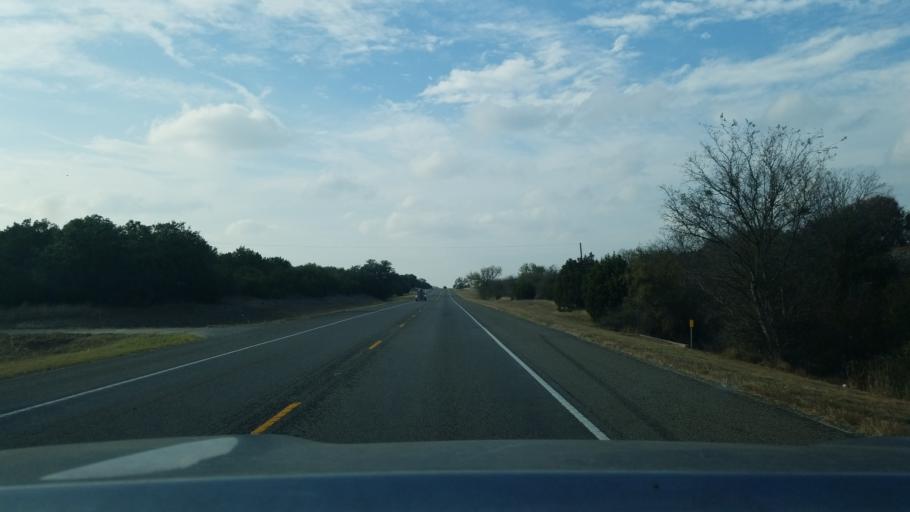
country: US
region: Texas
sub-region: Lampasas County
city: Lampasas
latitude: 31.1693
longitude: -98.3433
